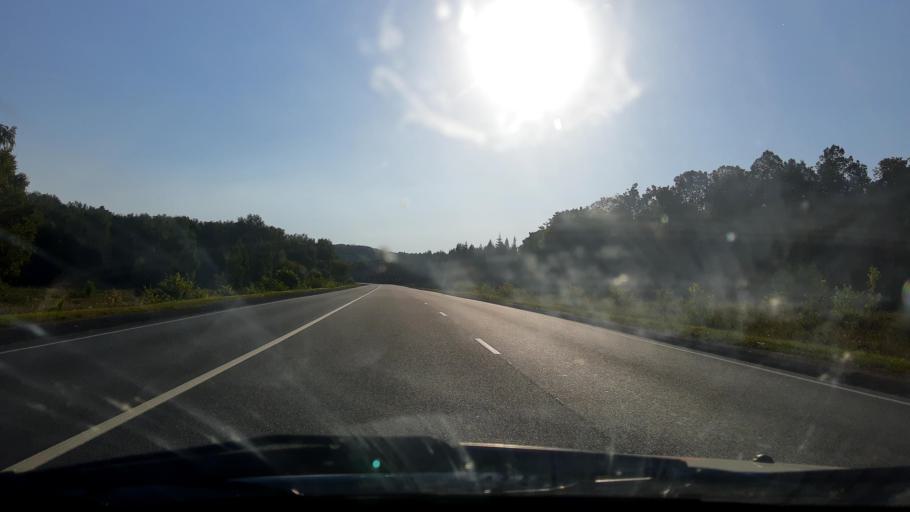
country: RU
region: Bashkortostan
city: Oktyabr'skiy
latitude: 54.4319
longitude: 53.4803
